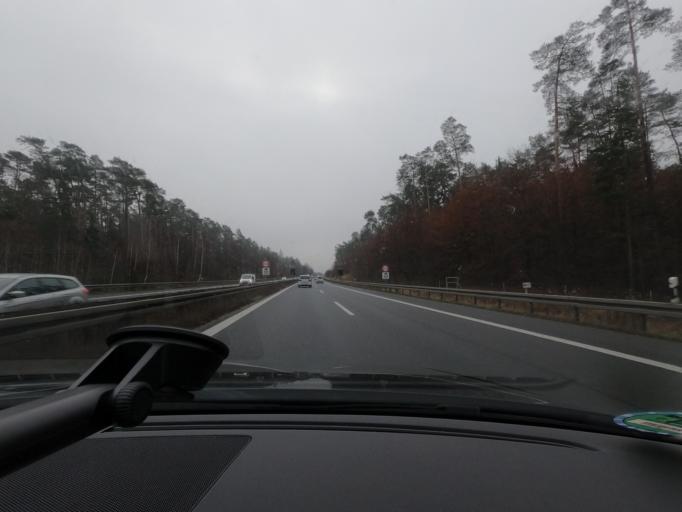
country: DE
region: Bavaria
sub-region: Upper Franconia
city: Memmelsdorf
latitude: 49.8957
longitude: 10.9486
